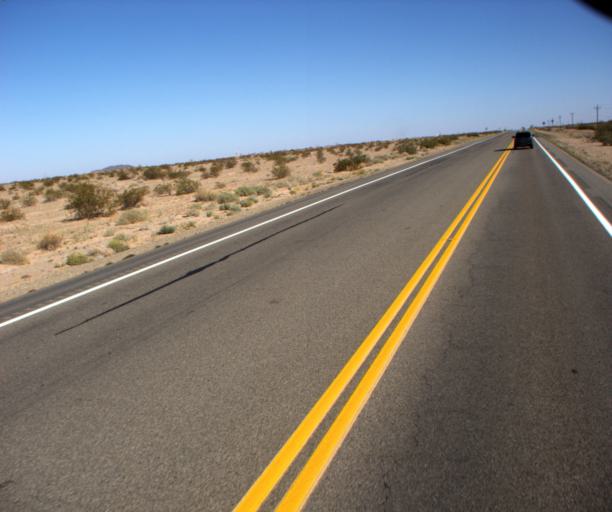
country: US
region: Arizona
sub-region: Yuma County
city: Fortuna Foothills
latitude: 32.8115
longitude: -114.3796
